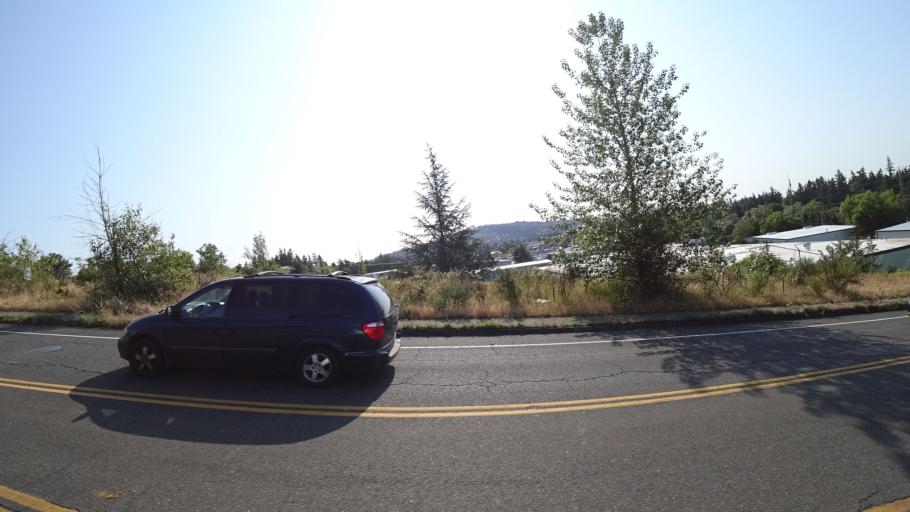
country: US
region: Oregon
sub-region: Multnomah County
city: Lents
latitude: 45.4573
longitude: -122.5990
